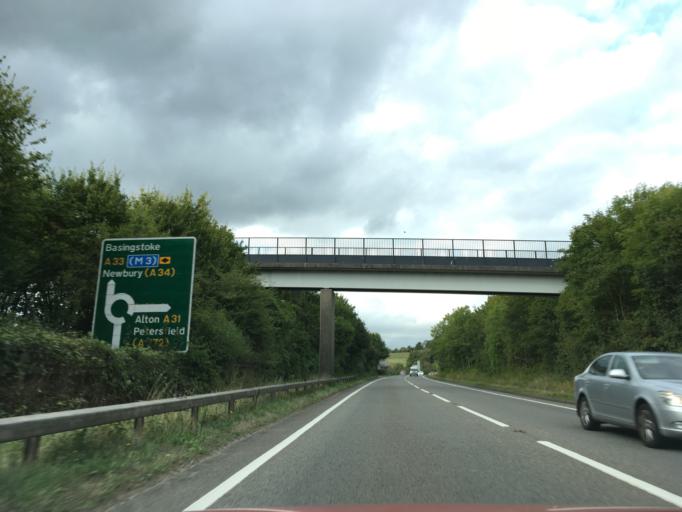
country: GB
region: England
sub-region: Hampshire
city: Winchester
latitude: 51.0570
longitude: -1.2932
